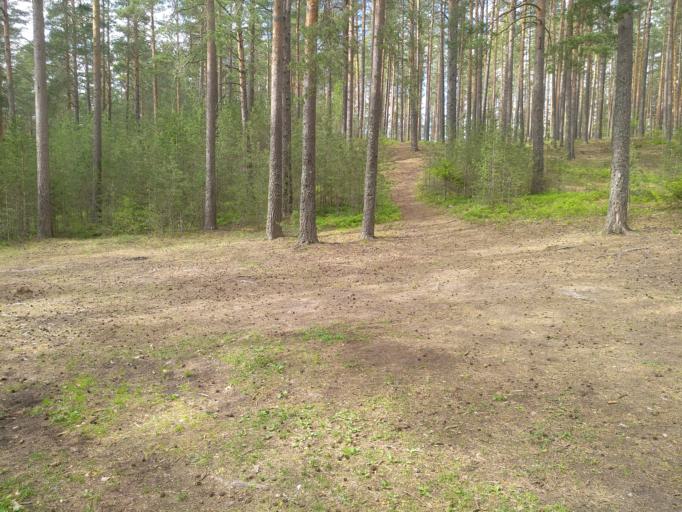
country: RU
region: Leningrad
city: Michurinskoye
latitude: 60.6018
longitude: 29.8722
